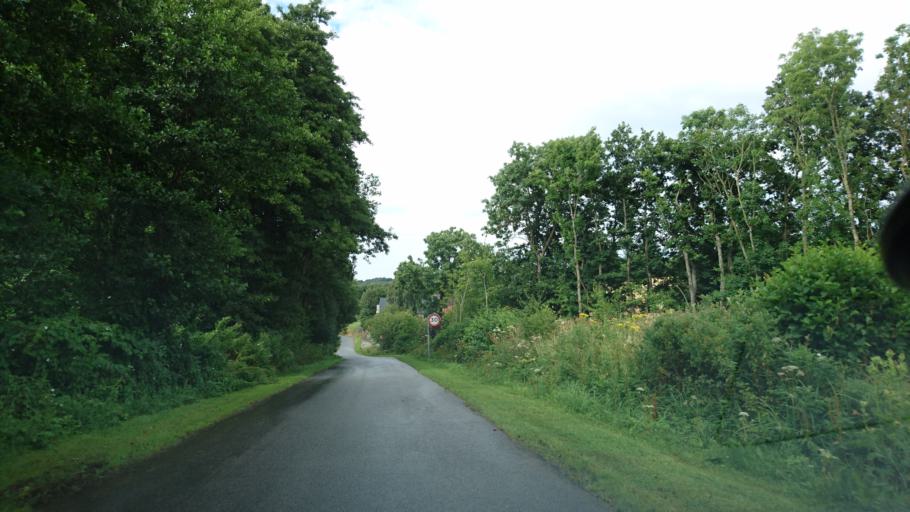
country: DK
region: North Denmark
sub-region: Frederikshavn Kommune
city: Frederikshavn
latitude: 57.3981
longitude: 10.4776
